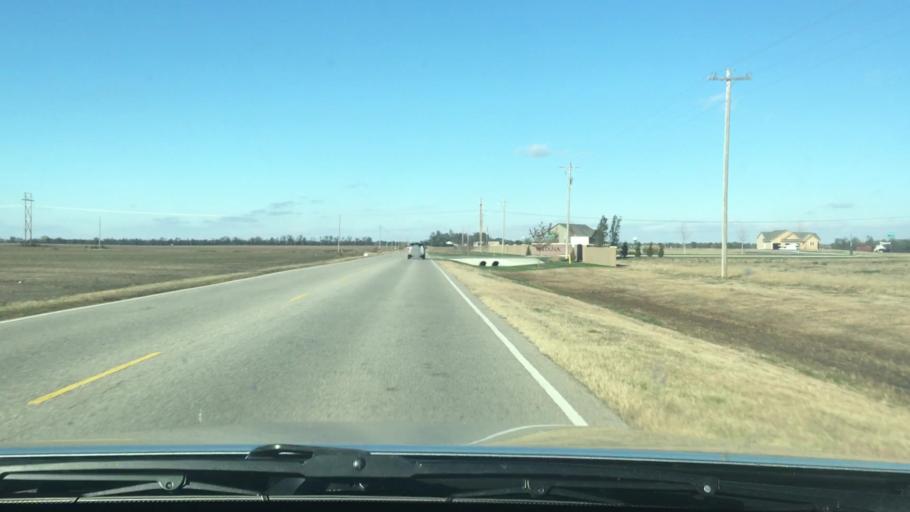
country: US
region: Kansas
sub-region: Sedgwick County
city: Maize
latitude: 37.7409
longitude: -97.4809
